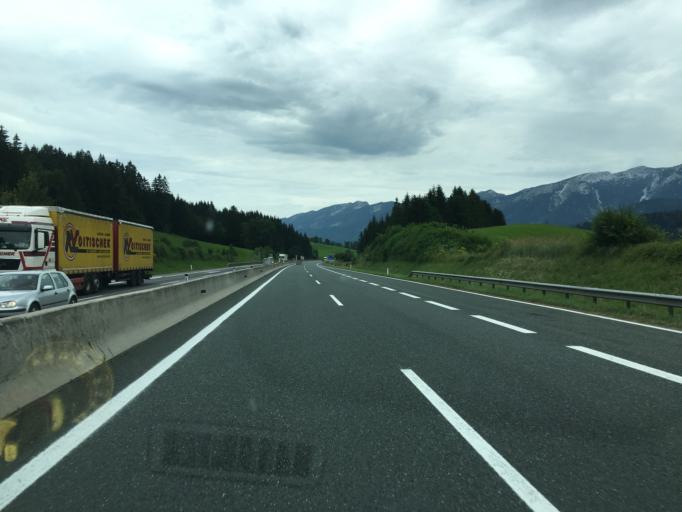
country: AT
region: Upper Austria
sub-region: Politischer Bezirk Kirchdorf an der Krems
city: Rossleithen
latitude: 47.6880
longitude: 14.3202
